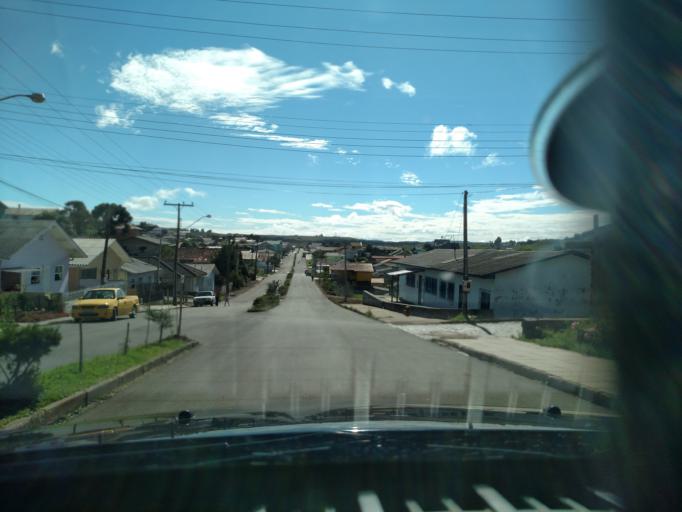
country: BR
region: Santa Catarina
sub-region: Sao Joaquim
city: Sao Joaquim
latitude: -28.2916
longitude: -49.9275
